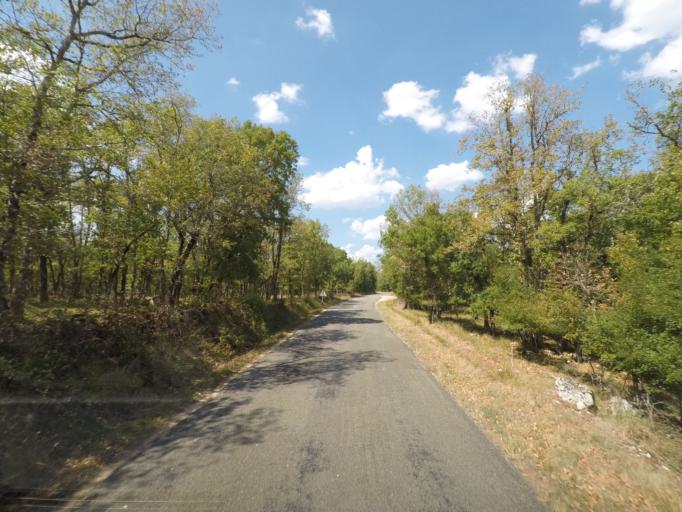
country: FR
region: Midi-Pyrenees
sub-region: Departement du Lot
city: Cahors
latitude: 44.5389
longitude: 1.5992
